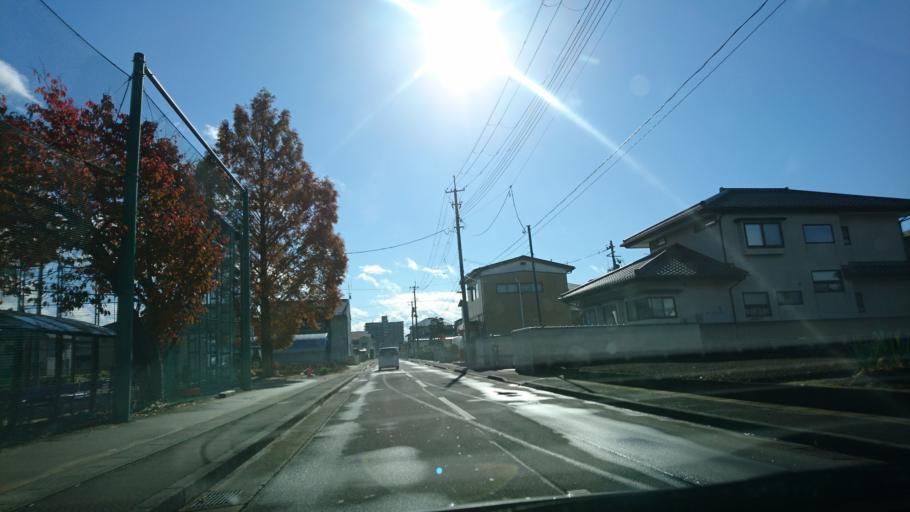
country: JP
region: Iwate
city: Ichinoseki
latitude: 38.9428
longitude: 141.1342
